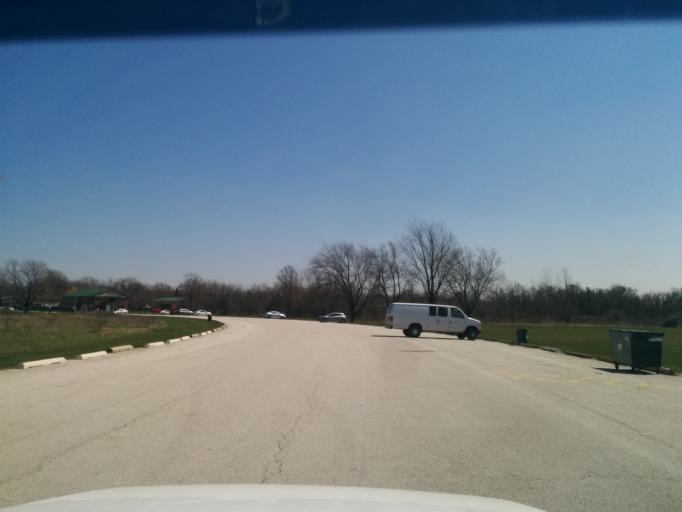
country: US
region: Illinois
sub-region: Cook County
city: Midlothian
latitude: 41.6079
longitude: -87.7199
